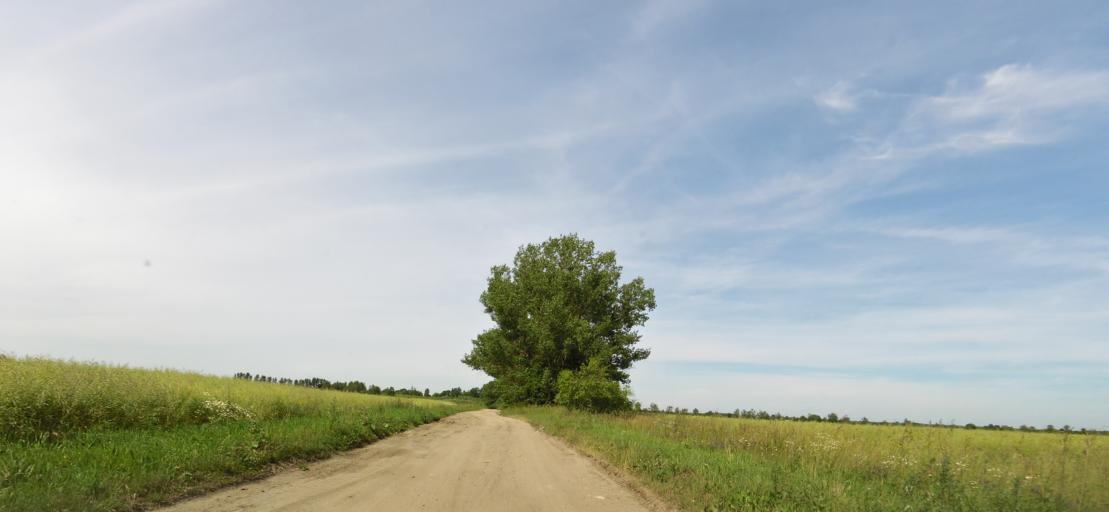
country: LT
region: Panevezys
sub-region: Panevezys City
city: Panevezys
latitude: 55.9102
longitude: 24.2907
